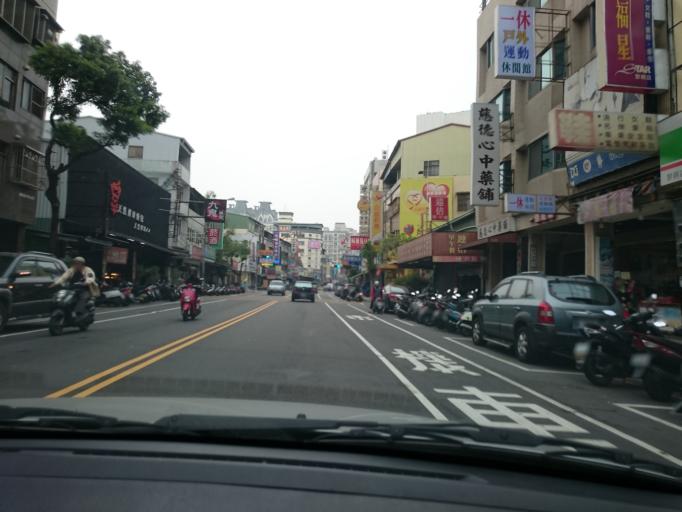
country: TW
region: Taiwan
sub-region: Taichung City
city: Taichung
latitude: 24.1471
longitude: 120.6361
